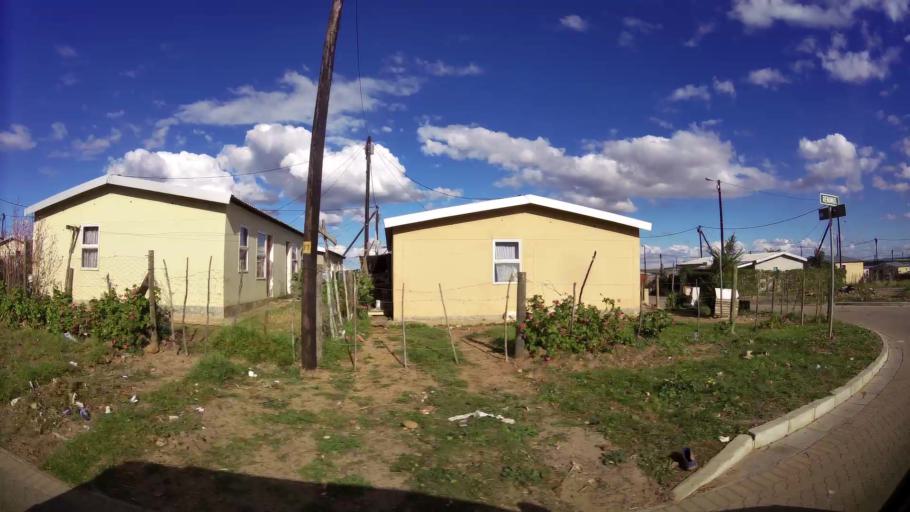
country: ZA
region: Western Cape
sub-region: Overberg District Municipality
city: Swellendam
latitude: -34.0481
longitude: 20.4406
